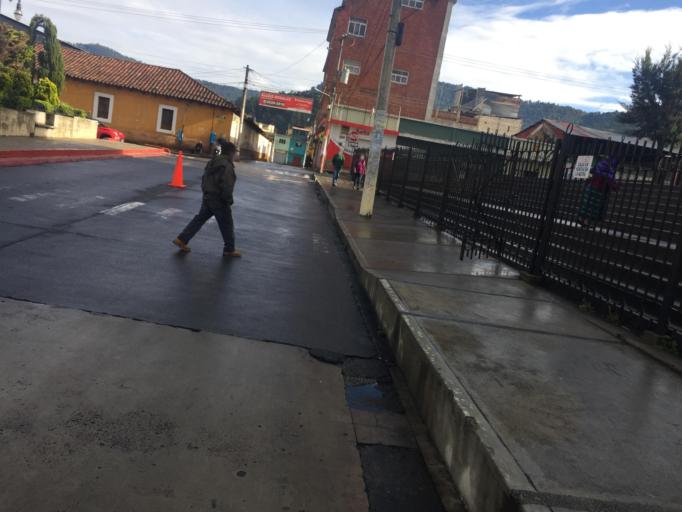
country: GT
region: Totonicapan
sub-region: Municipio de Totonicapan
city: Totonicapan
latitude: 14.9125
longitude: -91.3597
